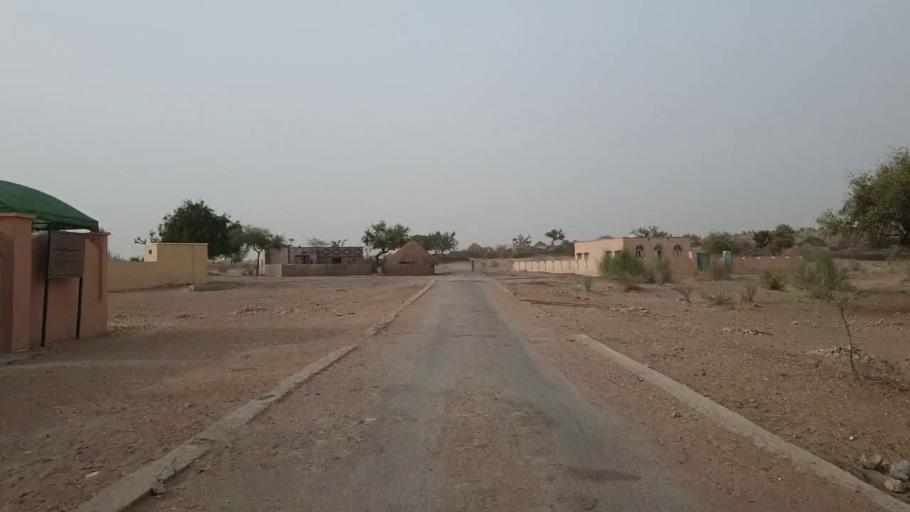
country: PK
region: Sindh
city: Islamkot
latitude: 24.5737
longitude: 70.3657
